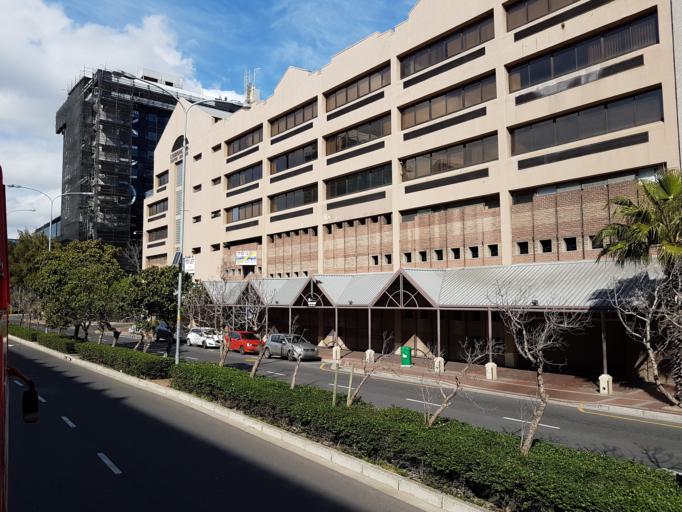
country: ZA
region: Western Cape
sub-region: City of Cape Town
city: Cape Town
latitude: -33.9165
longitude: 18.4267
